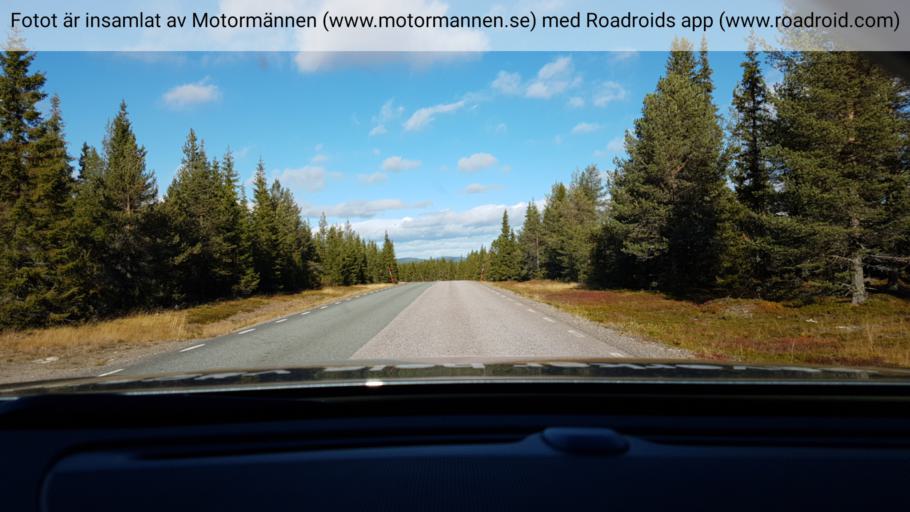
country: SE
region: Norrbotten
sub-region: Arjeplogs Kommun
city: Arjeplog
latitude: 65.8344
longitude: 18.4289
